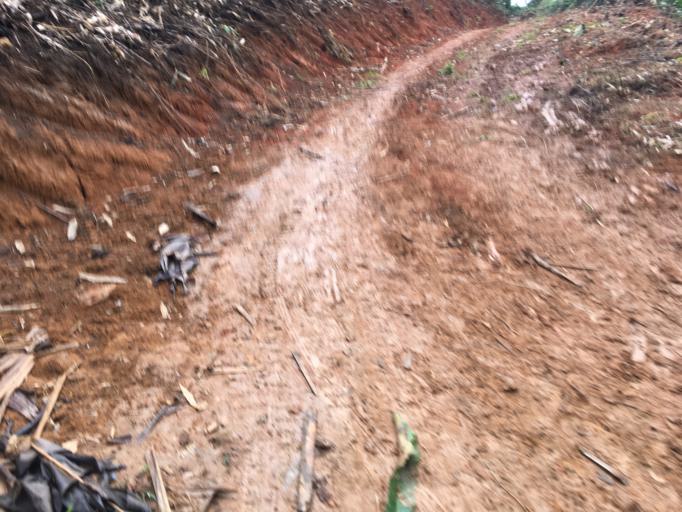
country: LA
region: Houaphan
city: Xamtay
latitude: 19.9017
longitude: 104.4594
